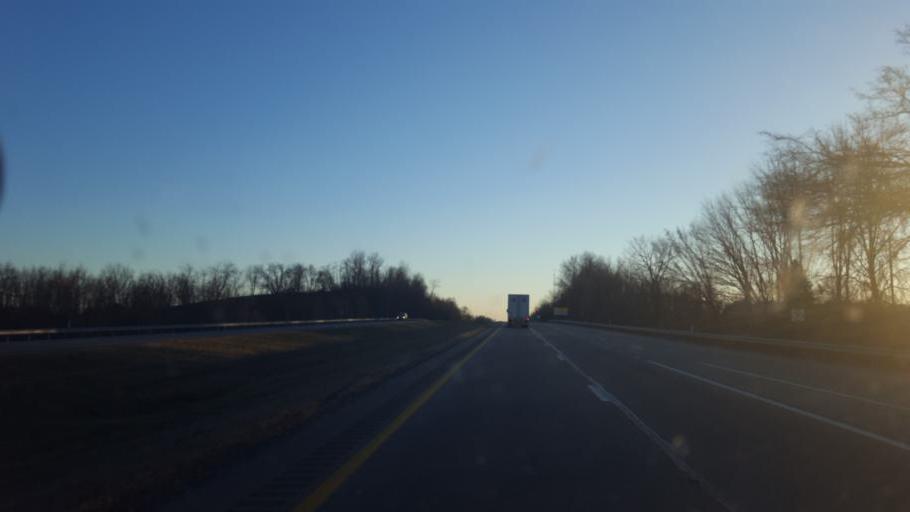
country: US
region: West Virginia
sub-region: Ohio County
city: West Liberty
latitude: 40.0893
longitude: -80.5384
